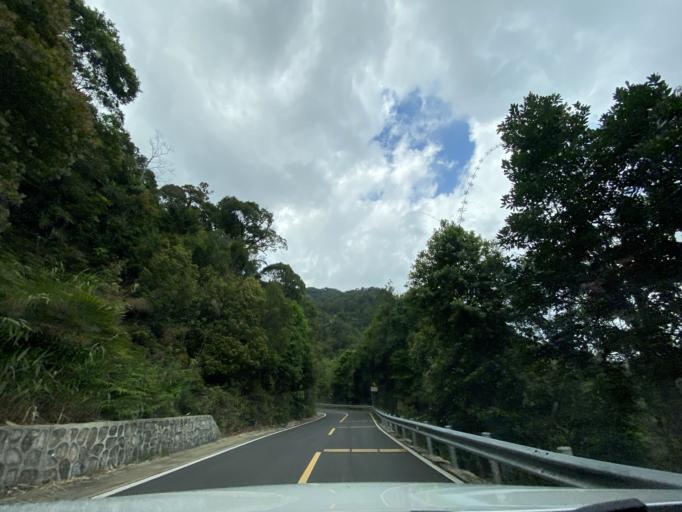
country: CN
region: Hainan
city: Benhao
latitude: 18.6803
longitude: 109.8793
